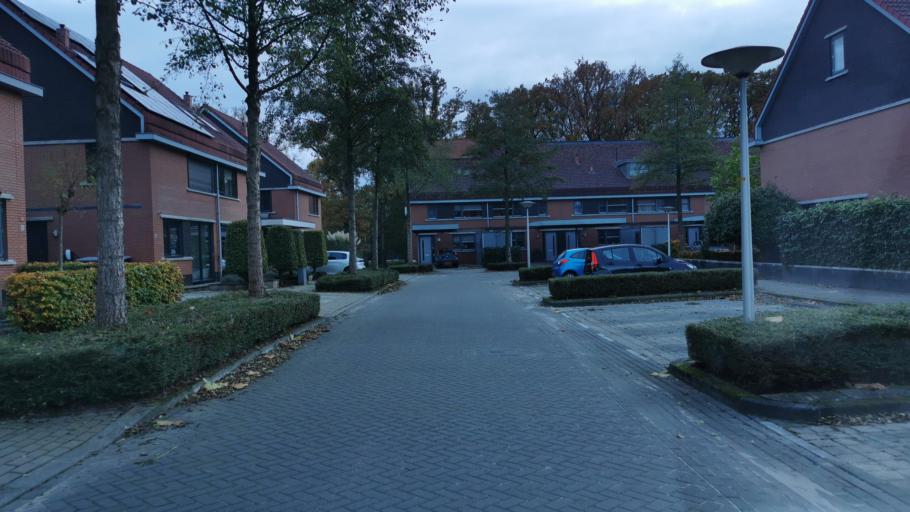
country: NL
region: Overijssel
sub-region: Gemeente Enschede
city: Enschede
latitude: 52.2187
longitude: 6.9384
